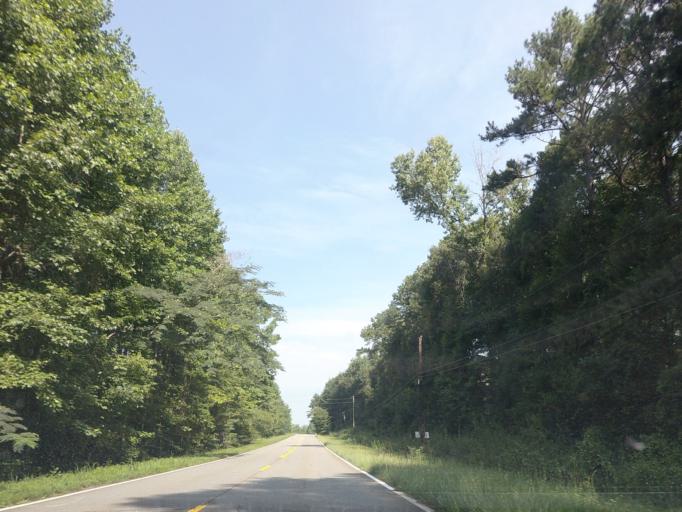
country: US
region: Georgia
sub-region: Bibb County
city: Macon
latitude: 32.9106
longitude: -83.6945
